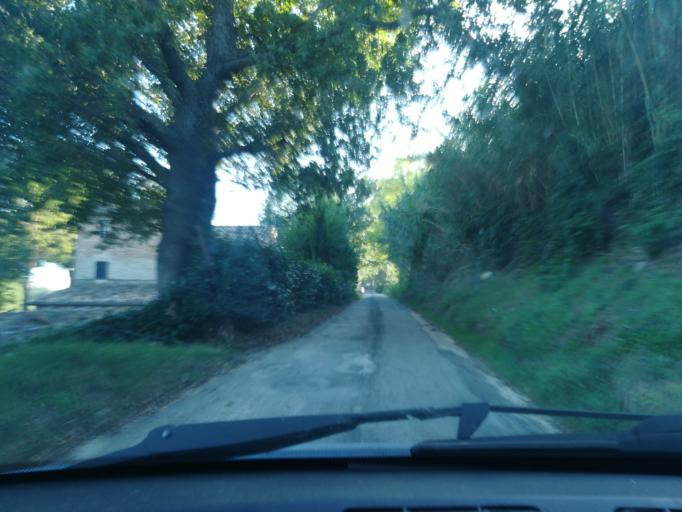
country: IT
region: The Marches
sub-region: Provincia di Macerata
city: Macerata
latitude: 43.2807
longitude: 13.4525
